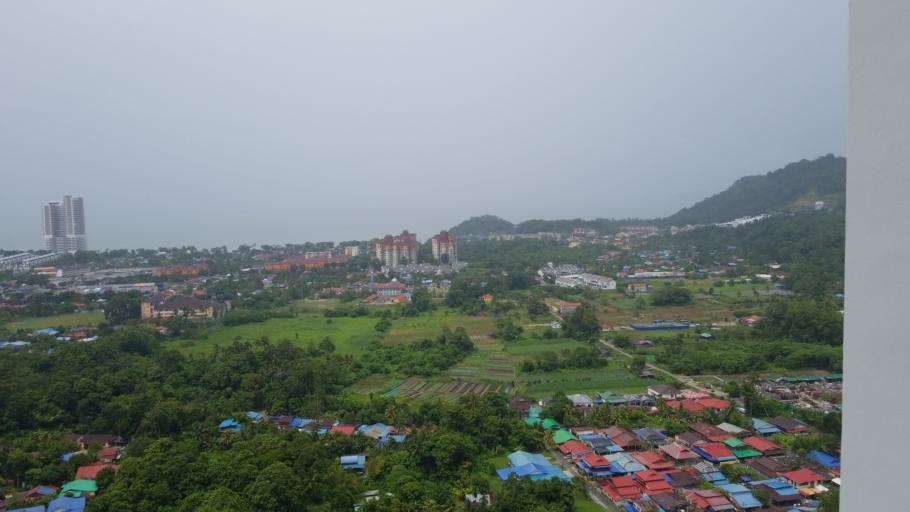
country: MY
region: Penang
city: Kampung Sungai Ara
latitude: 5.3020
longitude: 100.2296
